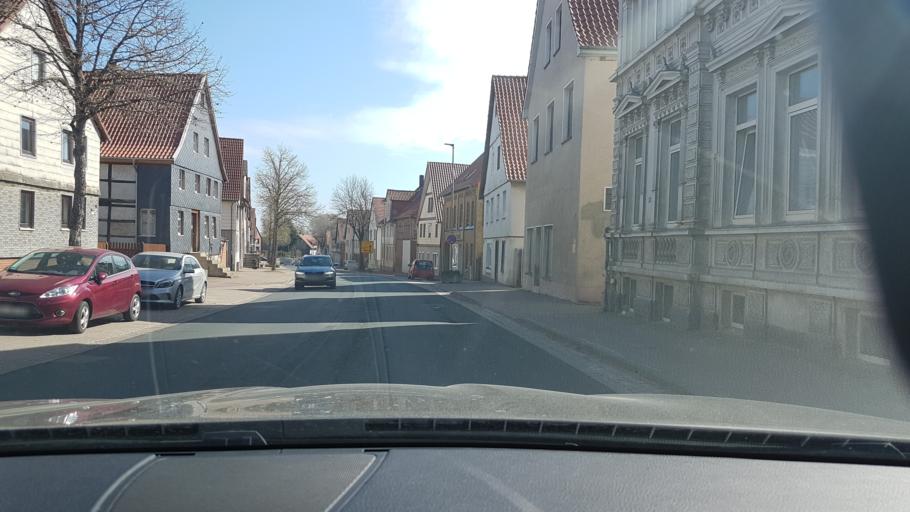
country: DE
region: Lower Saxony
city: Elze
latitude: 52.1887
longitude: 9.6740
